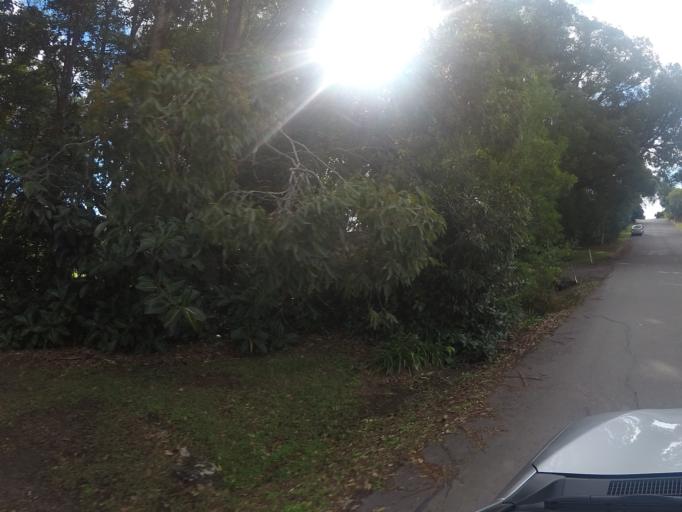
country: AU
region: Queensland
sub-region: Sunshine Coast
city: Nambour
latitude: -26.6199
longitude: 152.8621
